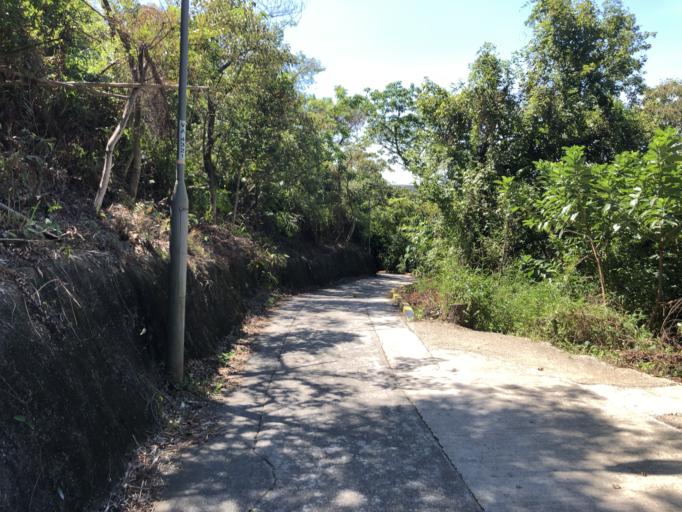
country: HK
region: Tuen Mun
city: Tuen Mun
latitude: 22.2943
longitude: 113.9732
